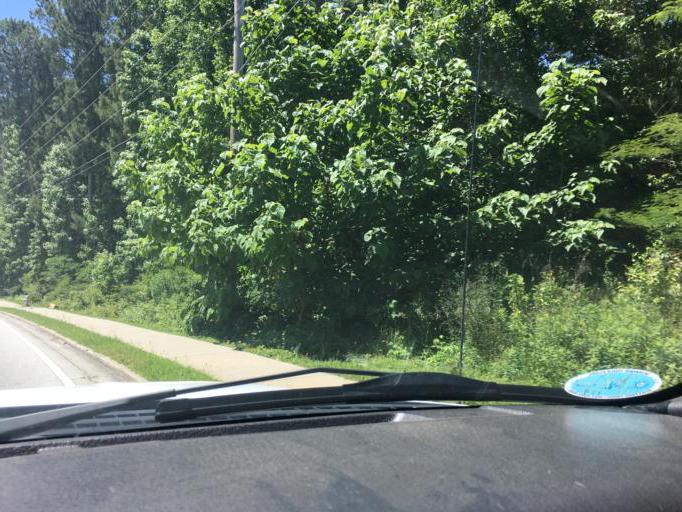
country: US
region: Georgia
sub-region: Gwinnett County
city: Mountain Park
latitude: 33.8270
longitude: -84.1148
